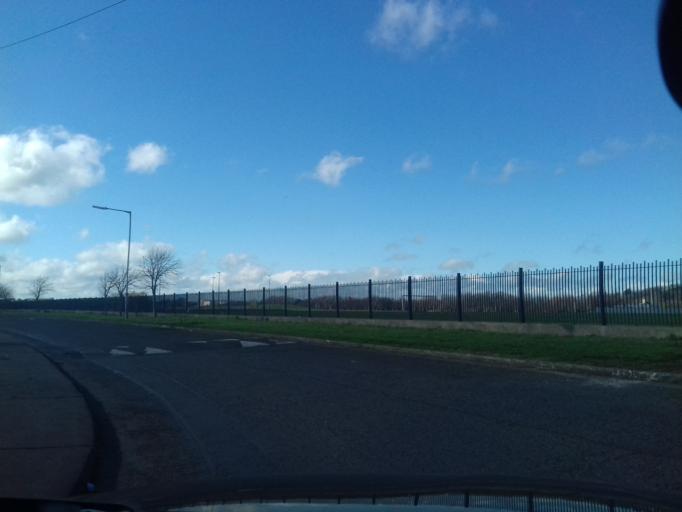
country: IE
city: Darndale
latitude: 53.4023
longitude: -6.1888
